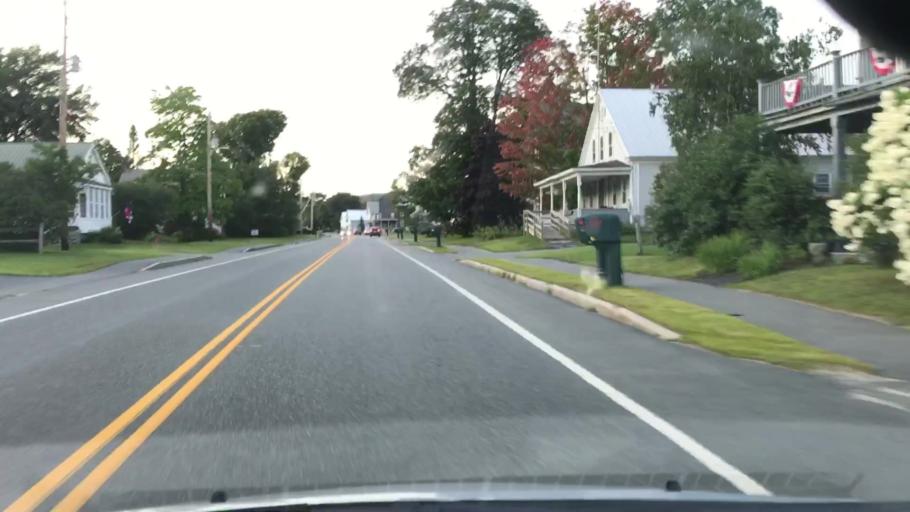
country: US
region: New Hampshire
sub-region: Grafton County
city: Rumney
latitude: 43.9166
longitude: -71.8882
